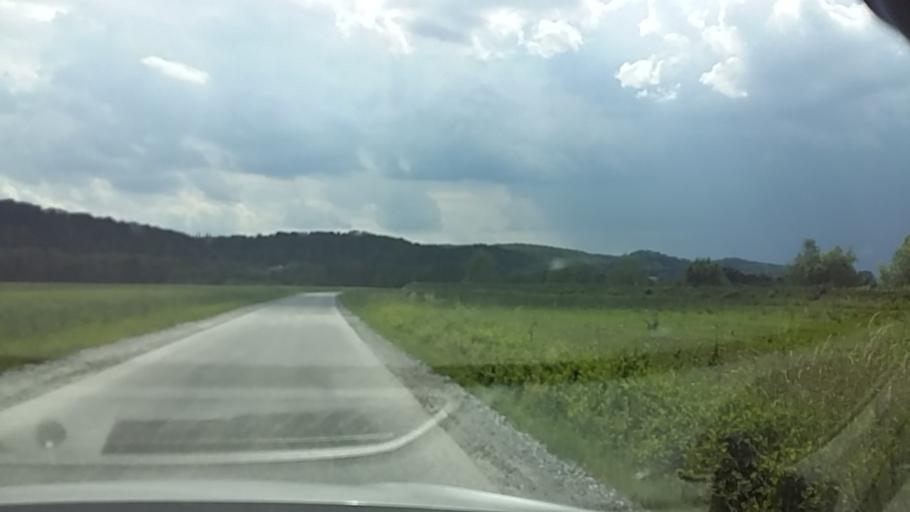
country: AT
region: Styria
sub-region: Politischer Bezirk Hartberg-Fuerstenfeld
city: Soechau
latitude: 47.0663
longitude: 16.0196
